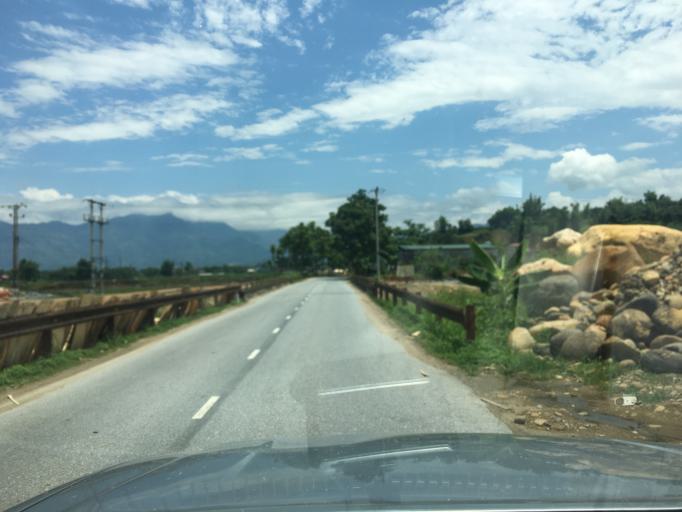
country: VN
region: Yen Bai
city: Son Thinh
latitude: 21.6222
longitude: 104.5093
